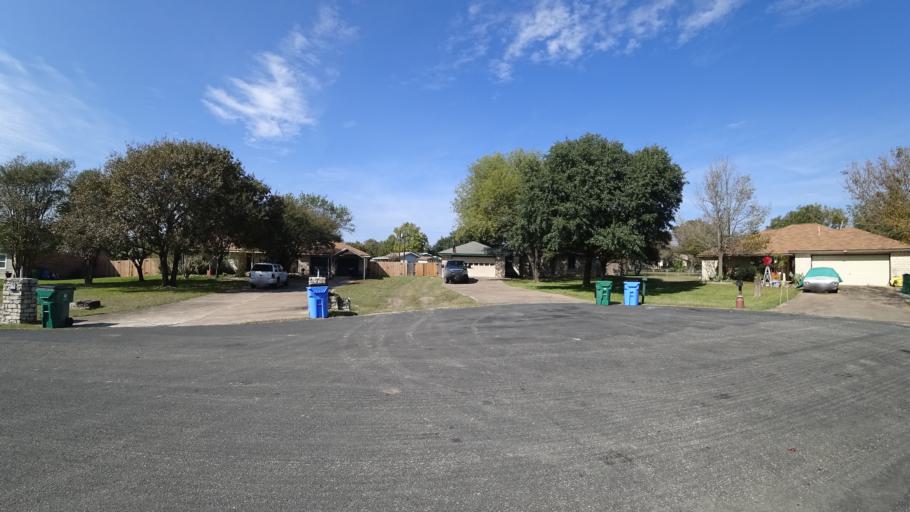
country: US
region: Texas
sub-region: Travis County
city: Pflugerville
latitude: 30.4130
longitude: -97.6253
